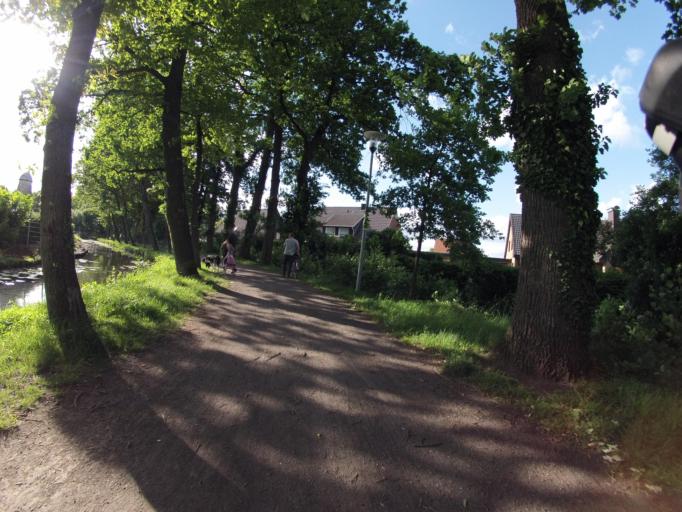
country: DE
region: North Rhine-Westphalia
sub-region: Regierungsbezirk Munster
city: Horstel
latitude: 52.2742
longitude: 7.5819
